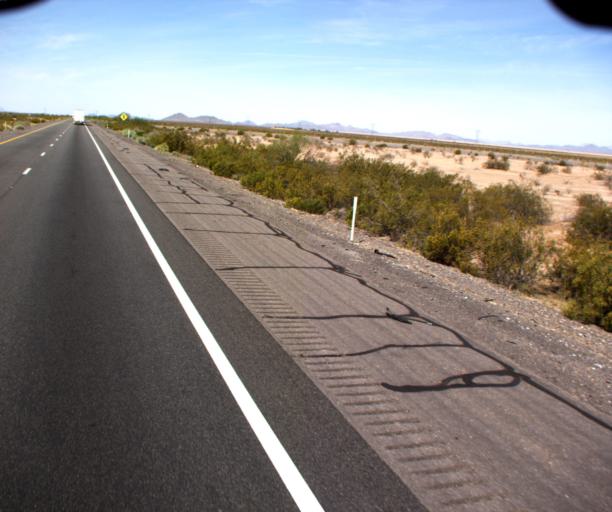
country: US
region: Arizona
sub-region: La Paz County
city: Salome
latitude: 33.5693
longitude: -113.3529
